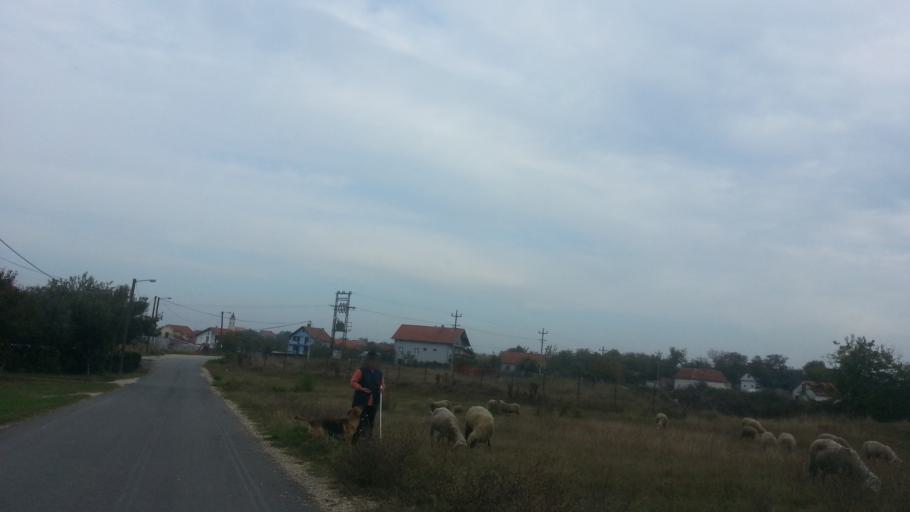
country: RS
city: Surduk
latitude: 45.0633
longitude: 20.3265
